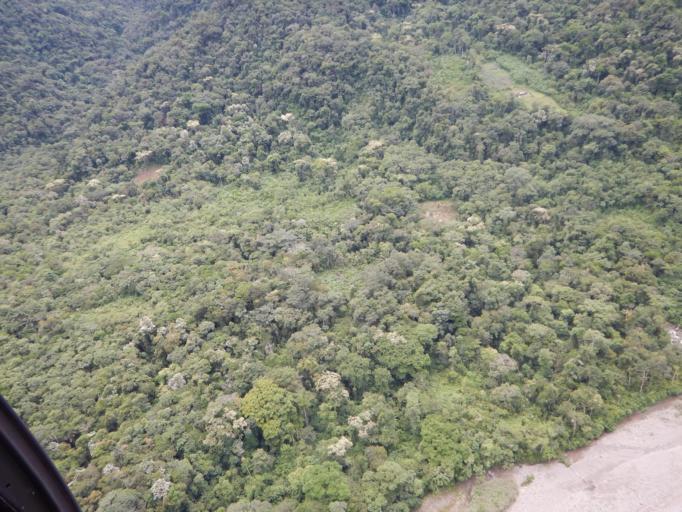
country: BO
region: Cochabamba
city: Totora
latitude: -17.4462
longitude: -65.0107
